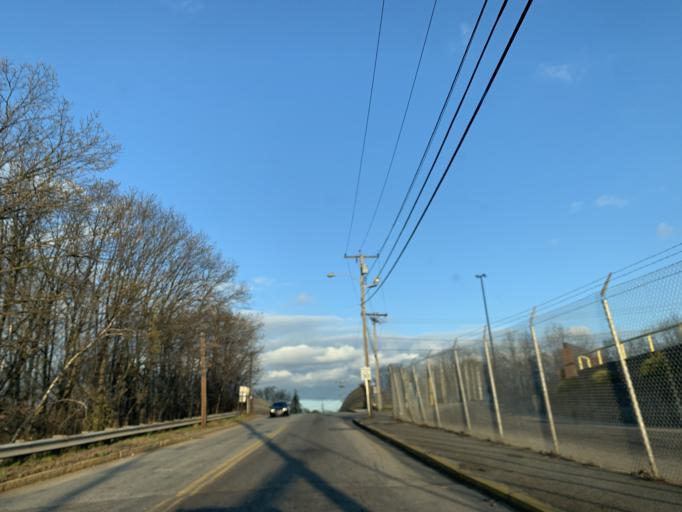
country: US
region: Rhode Island
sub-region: Providence County
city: Valley Falls
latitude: 41.8973
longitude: -71.3745
